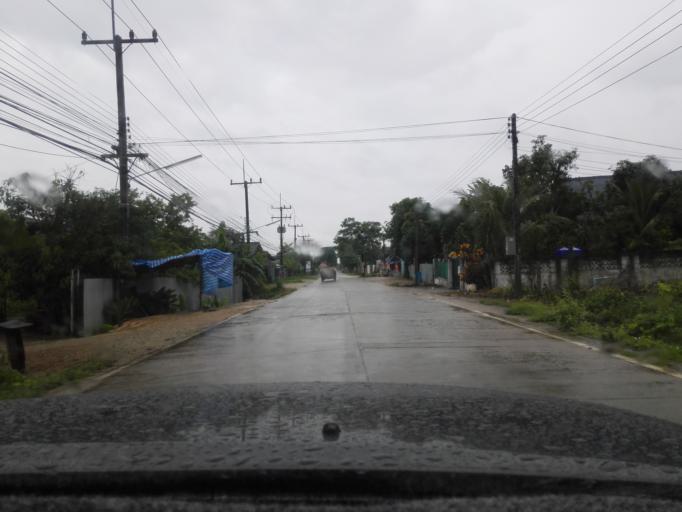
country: TH
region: Tak
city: Mae Sot
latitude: 16.6943
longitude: 98.5745
